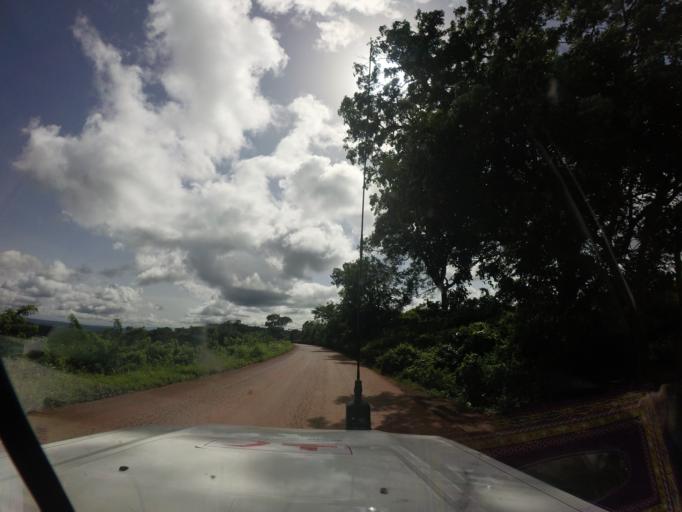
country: GN
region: Mamou
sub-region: Mamou Prefecture
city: Mamou
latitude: 10.3660
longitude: -12.1480
